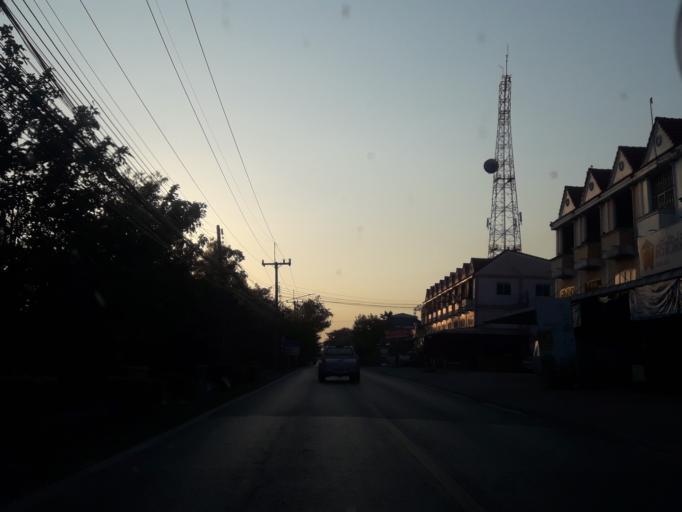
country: TH
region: Pathum Thani
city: Nong Suea
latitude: 14.1321
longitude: 100.8195
